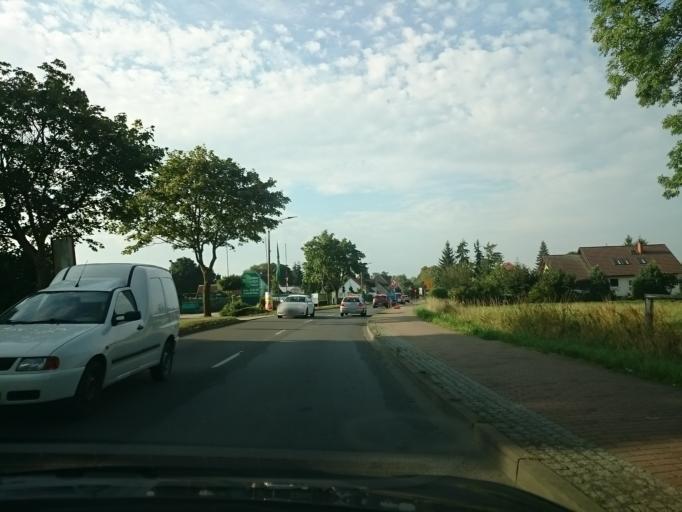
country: DE
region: Mecklenburg-Vorpommern
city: Demmin
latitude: 53.8960
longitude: 13.0408
